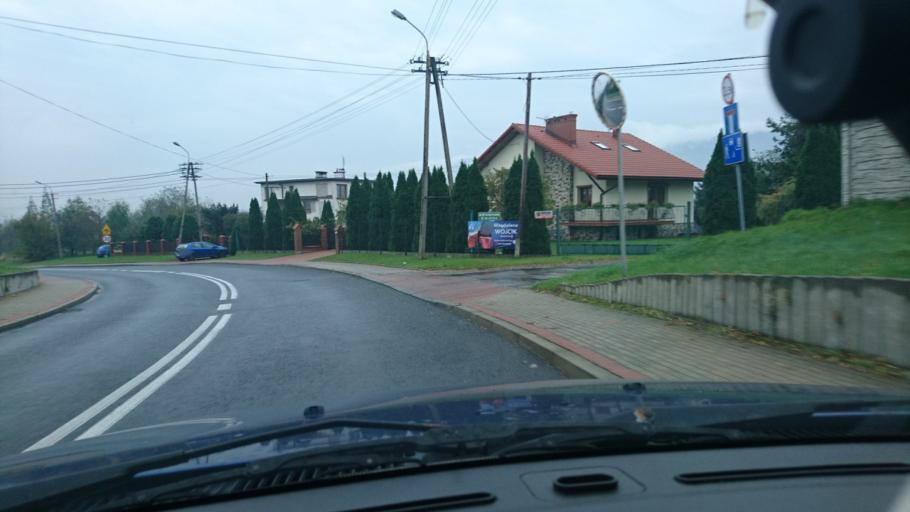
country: PL
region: Silesian Voivodeship
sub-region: Powiat bielski
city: Kozy
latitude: 49.8410
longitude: 19.1075
